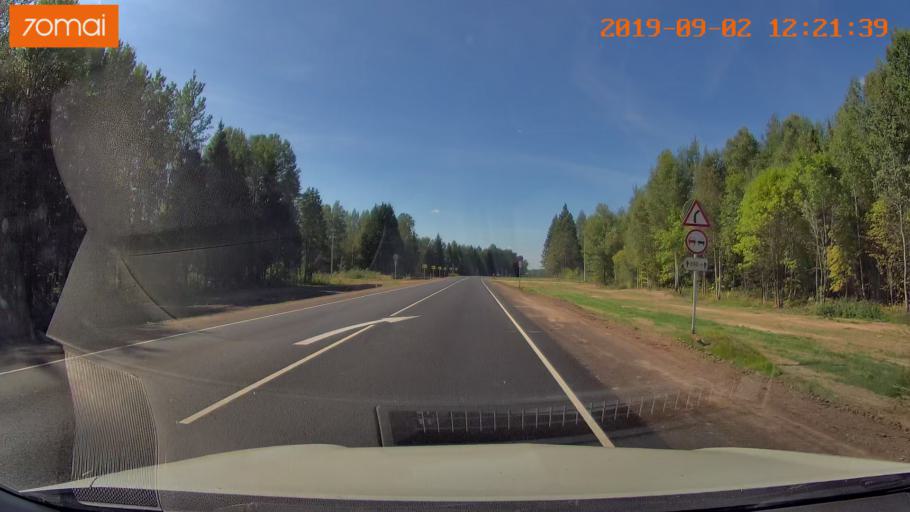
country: RU
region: Smolensk
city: Oster
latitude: 53.8862
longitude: 32.6511
